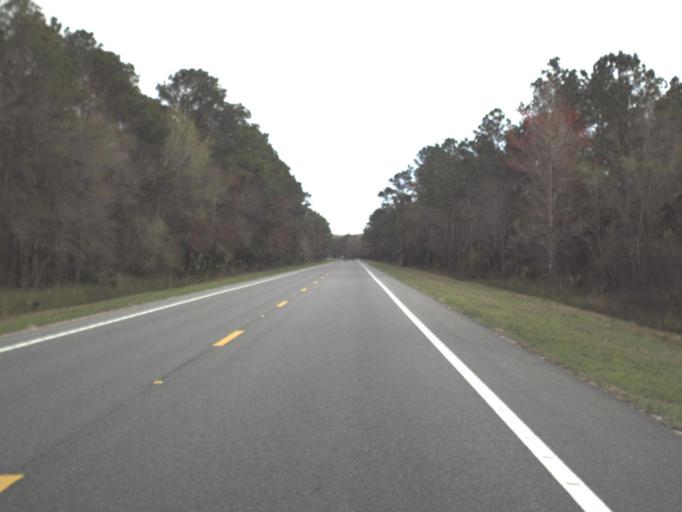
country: US
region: Florida
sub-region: Leon County
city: Woodville
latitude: 30.1697
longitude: -84.0070
